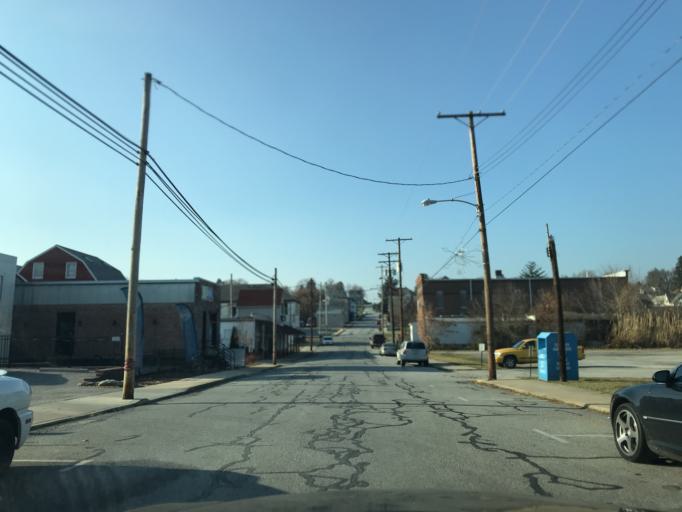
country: US
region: Pennsylvania
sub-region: York County
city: New Freedom
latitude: 39.7389
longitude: -76.6995
